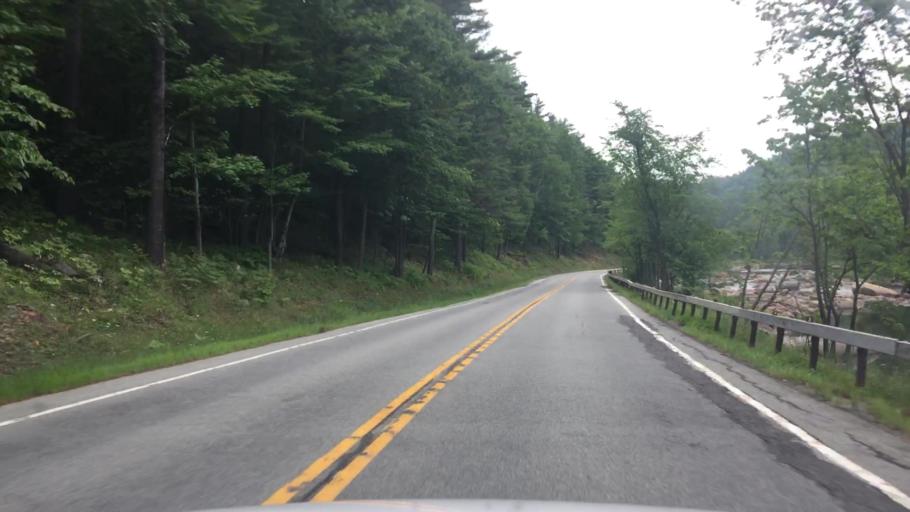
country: US
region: New York
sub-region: Essex County
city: Keeseville
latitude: 44.4227
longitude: -73.6815
